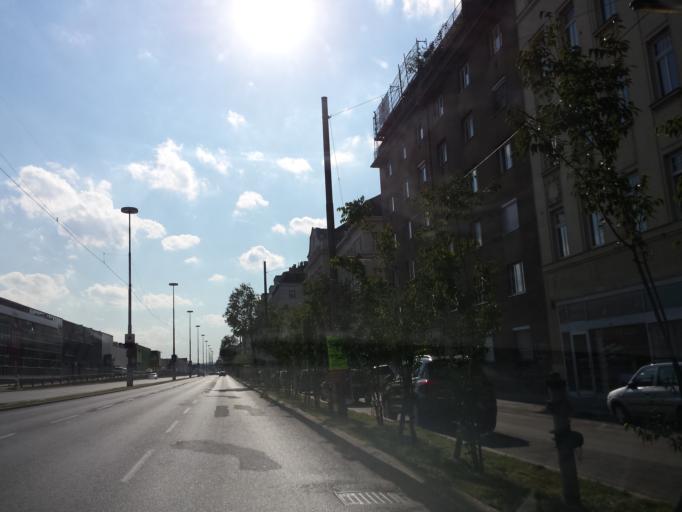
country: AT
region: Vienna
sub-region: Wien Stadt
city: Vienna
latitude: 48.1849
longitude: 16.3700
